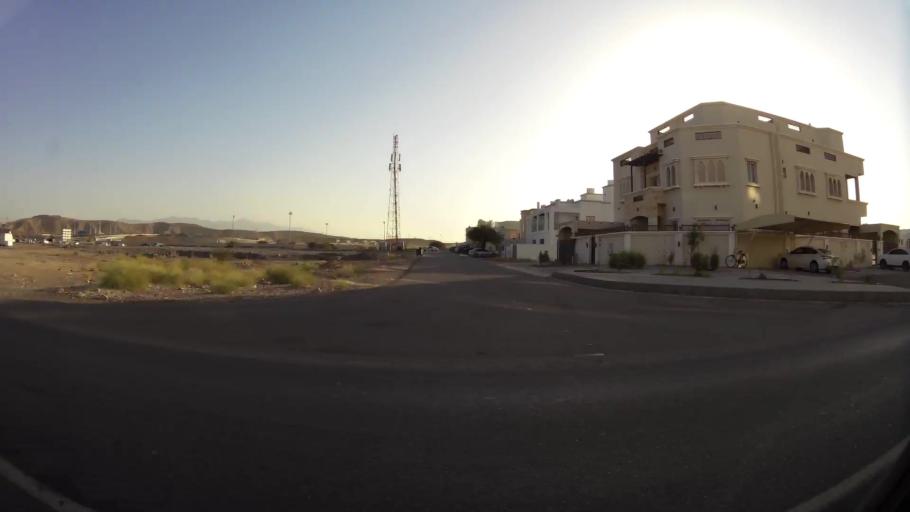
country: OM
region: Muhafazat Masqat
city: As Sib al Jadidah
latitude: 23.5863
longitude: 58.1456
